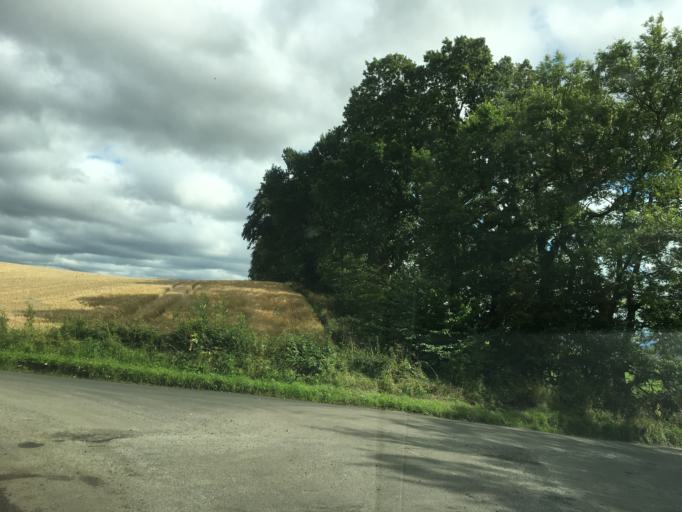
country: GB
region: Scotland
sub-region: West Lothian
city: Linlithgow
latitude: 55.9946
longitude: -3.5813
